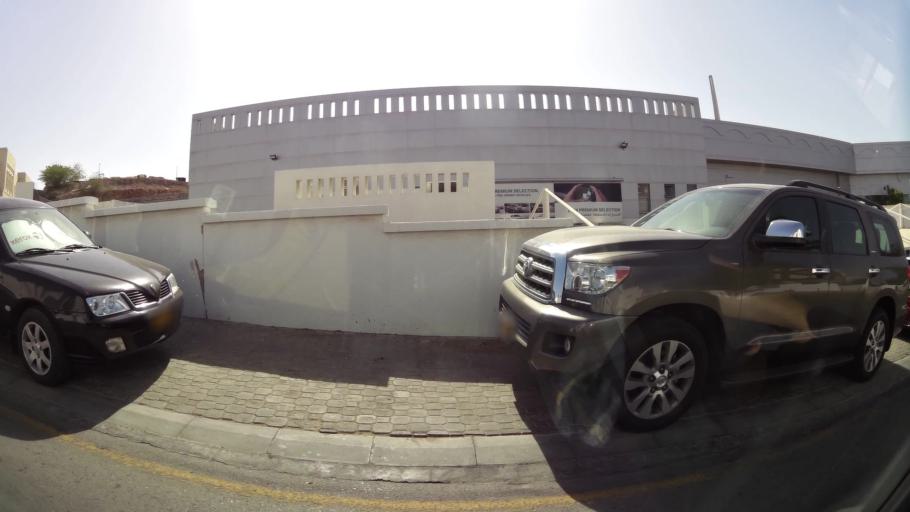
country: OM
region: Muhafazat Masqat
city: Muscat
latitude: 23.6086
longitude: 58.4948
